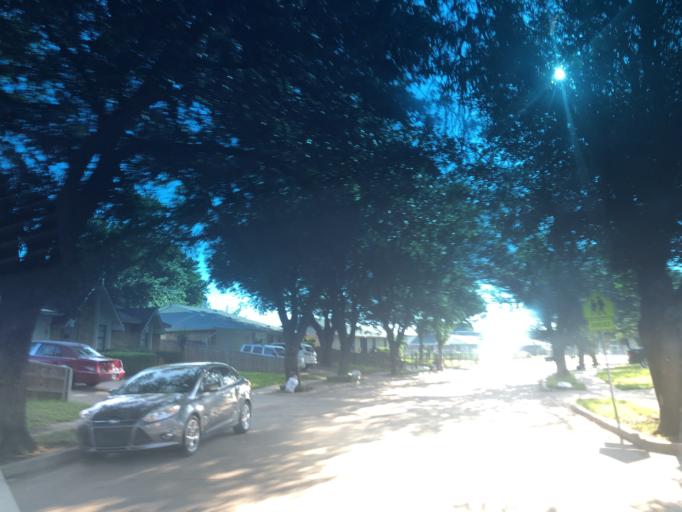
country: US
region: Texas
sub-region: Dallas County
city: Grand Prairie
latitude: 32.7017
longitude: -96.9997
